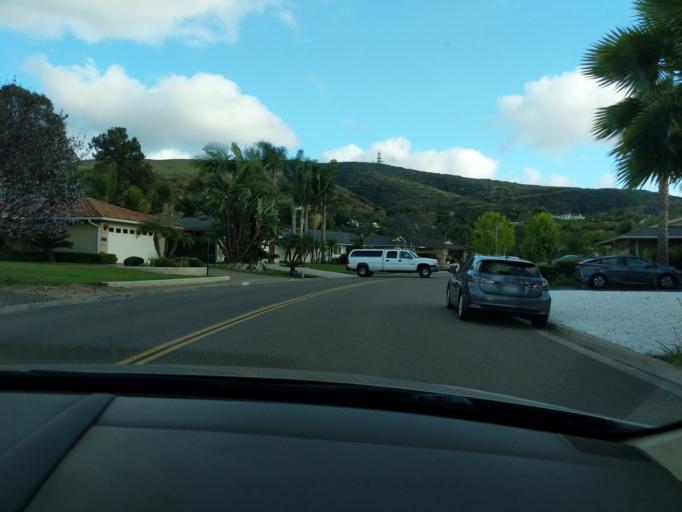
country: US
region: California
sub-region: San Diego County
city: Lake San Marcos
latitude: 33.1218
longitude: -117.2031
